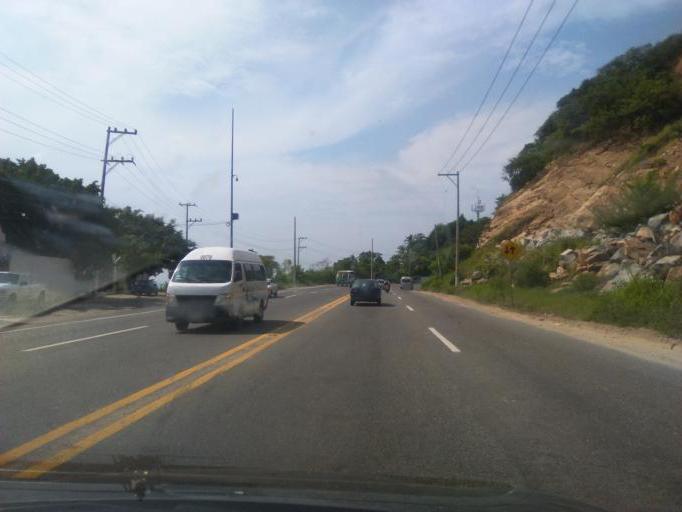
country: MX
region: Guerrero
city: Acapulco de Juarez
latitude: 16.8695
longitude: -99.9353
